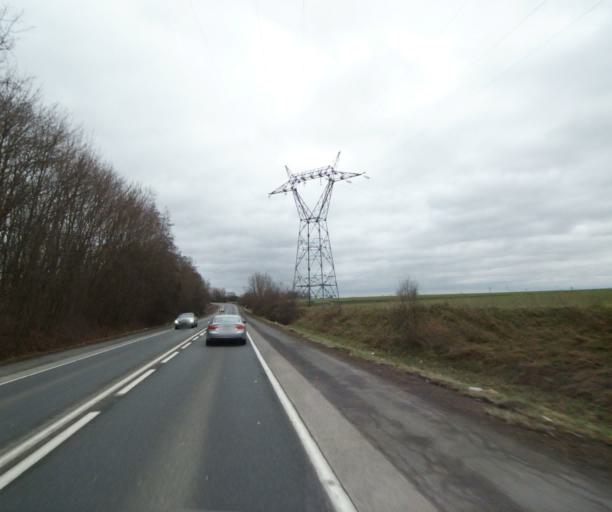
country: FR
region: Nord-Pas-de-Calais
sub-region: Departement du Nord
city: Saint-Saulve
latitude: 50.3697
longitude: 3.5687
